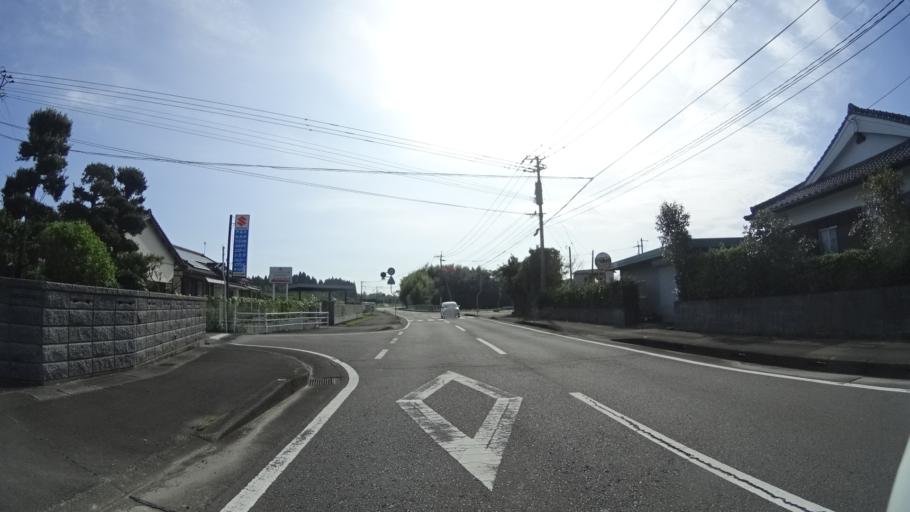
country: JP
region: Kagoshima
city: Okuchi-shinohara
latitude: 32.0415
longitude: 130.7873
